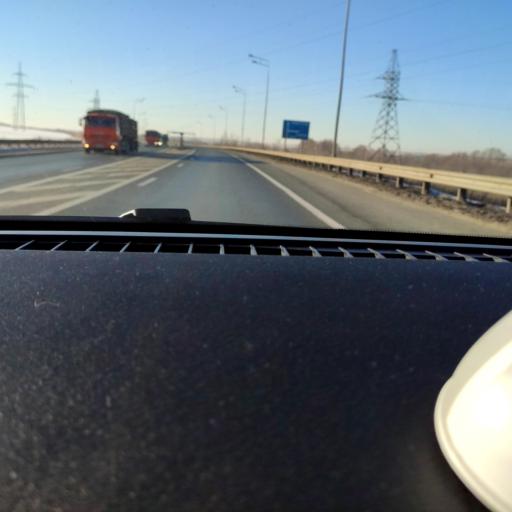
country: RU
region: Samara
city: Smyshlyayevka
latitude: 53.1407
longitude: 50.4368
